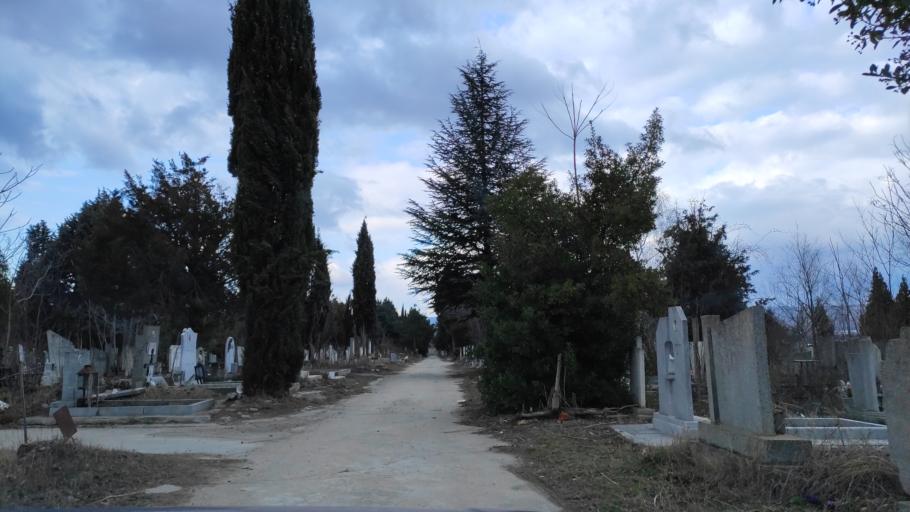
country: BG
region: Varna
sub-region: Obshtina Aksakovo
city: Aksakovo
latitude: 43.2214
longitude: 27.8103
